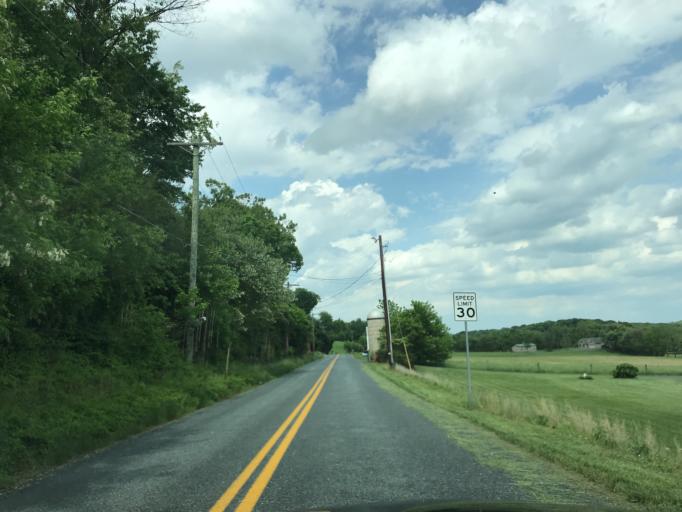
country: US
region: Pennsylvania
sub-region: York County
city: Susquehanna Trails
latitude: 39.6940
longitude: -76.3462
